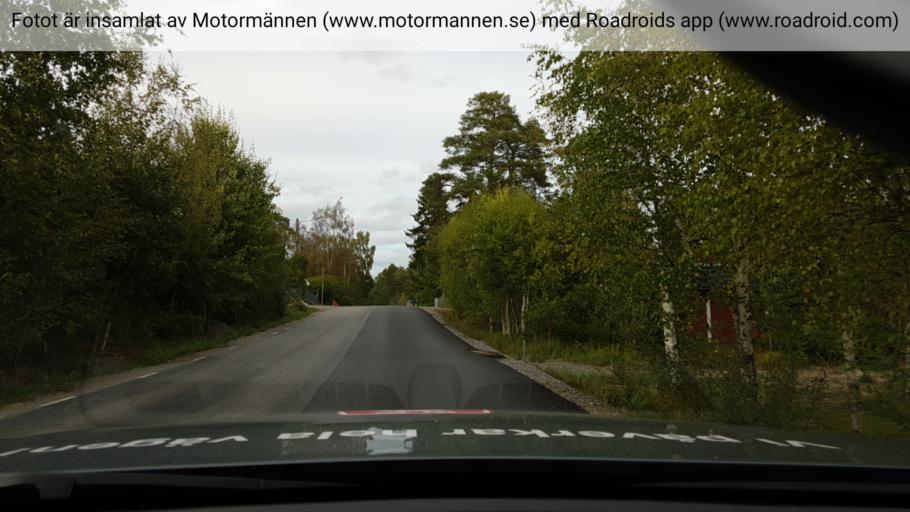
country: SE
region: Stockholm
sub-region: Haninge Kommun
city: Haninge
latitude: 59.0858
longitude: 18.1781
